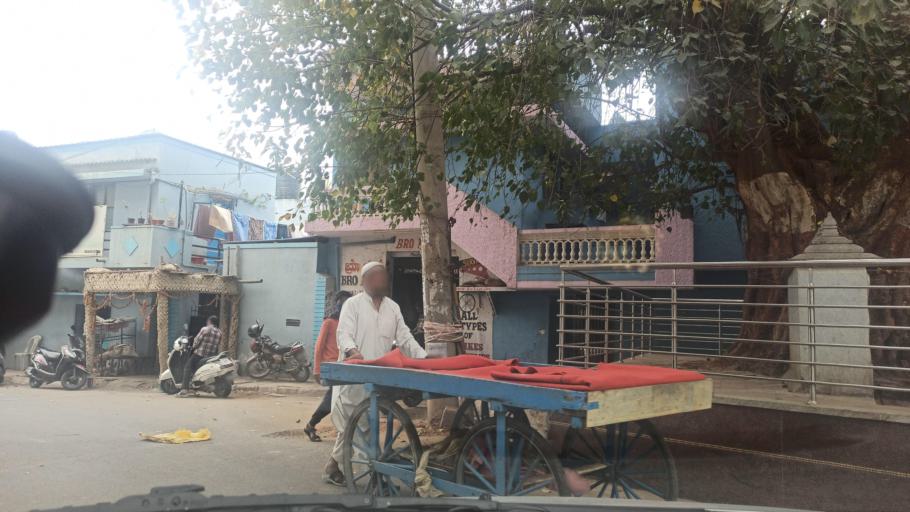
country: IN
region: Karnataka
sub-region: Bangalore Urban
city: Yelahanka
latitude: 13.0395
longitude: 77.6050
